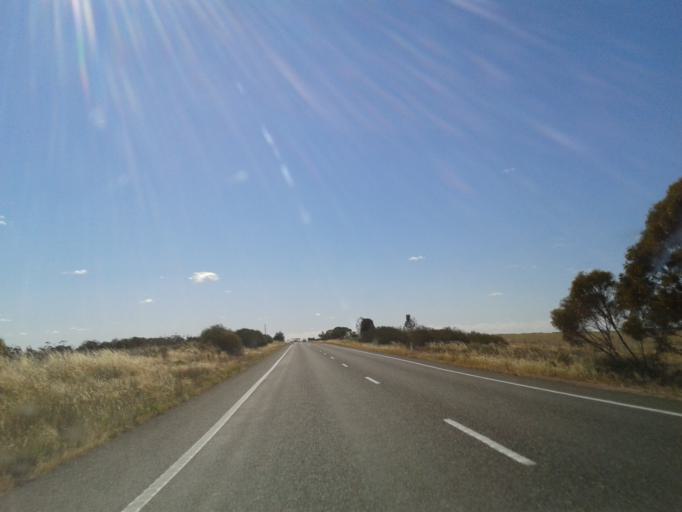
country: AU
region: South Australia
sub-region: Renmark Paringa
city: Renmark
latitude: -34.2750
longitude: 141.1878
